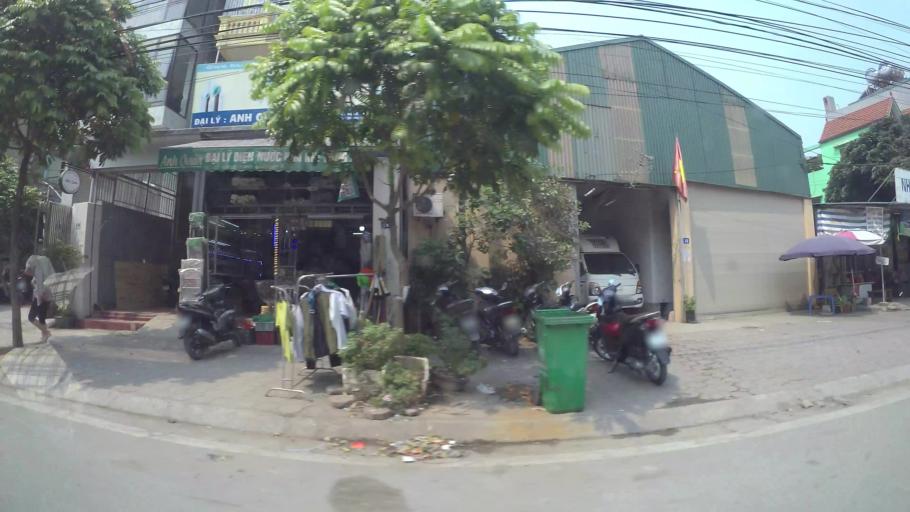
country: VN
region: Ha Noi
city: Van Dien
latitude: 20.9643
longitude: 105.8210
